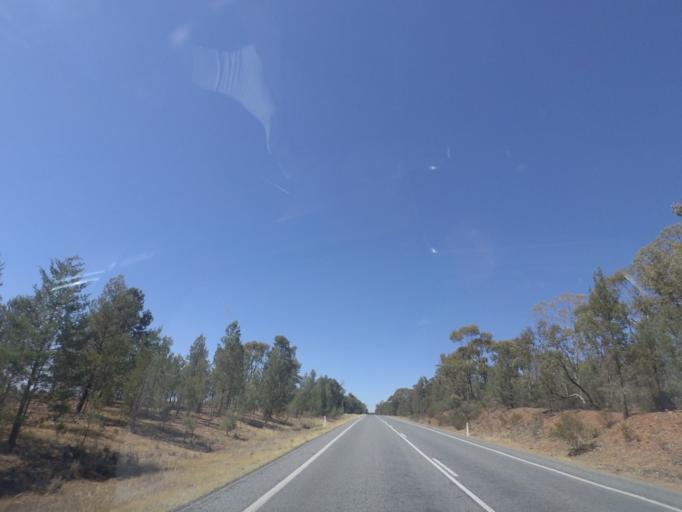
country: AU
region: New South Wales
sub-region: Narrandera
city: Narrandera
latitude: -34.4312
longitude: 146.8432
